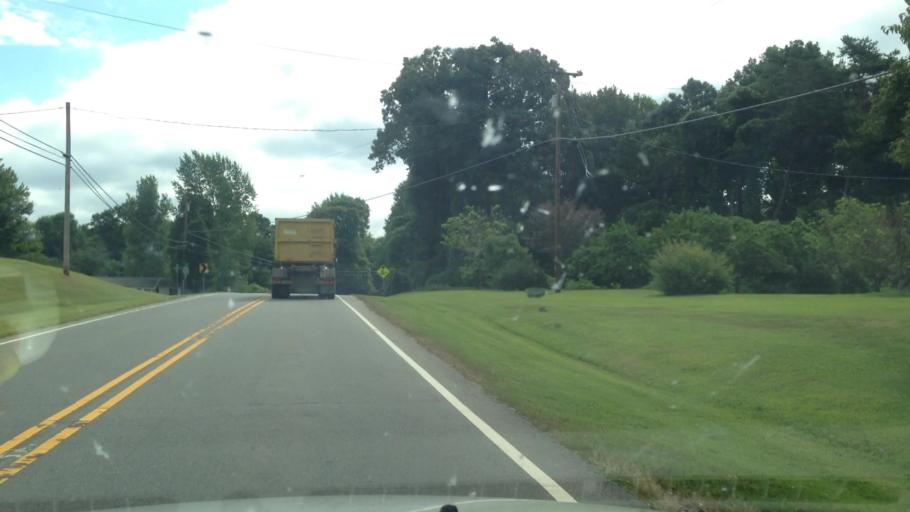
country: US
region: North Carolina
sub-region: Rockingham County
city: Wentworth
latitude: 36.3977
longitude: -79.7613
